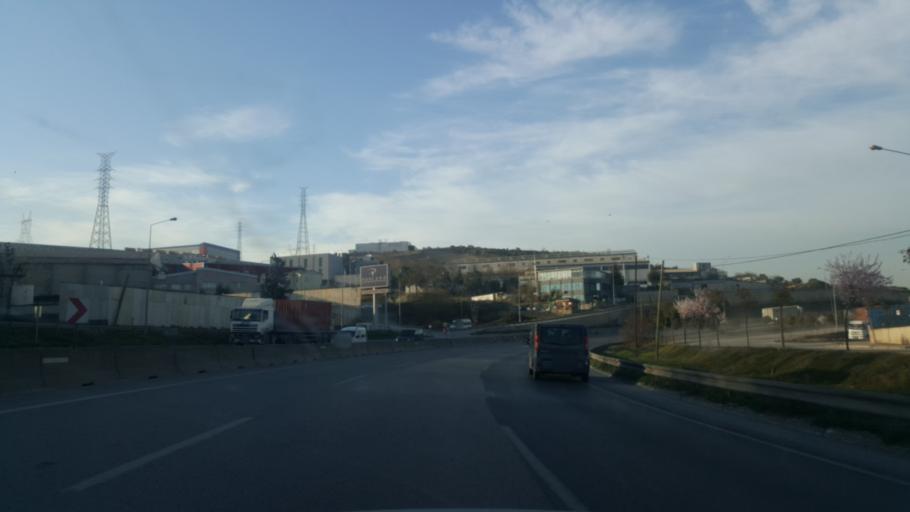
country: TR
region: Kocaeli
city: Tavsanli
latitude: 40.7973
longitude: 29.5252
